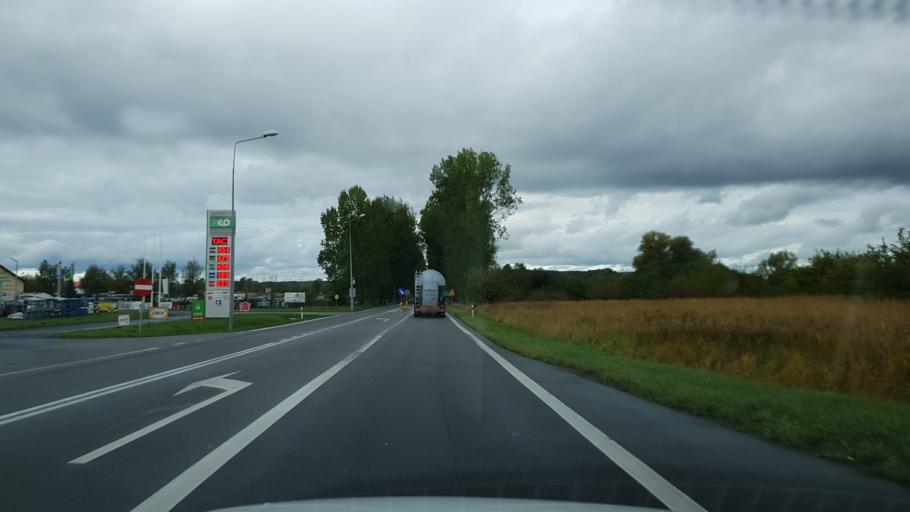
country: PL
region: West Pomeranian Voivodeship
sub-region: Powiat kamienski
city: Wolin
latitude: 53.8493
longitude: 14.6010
